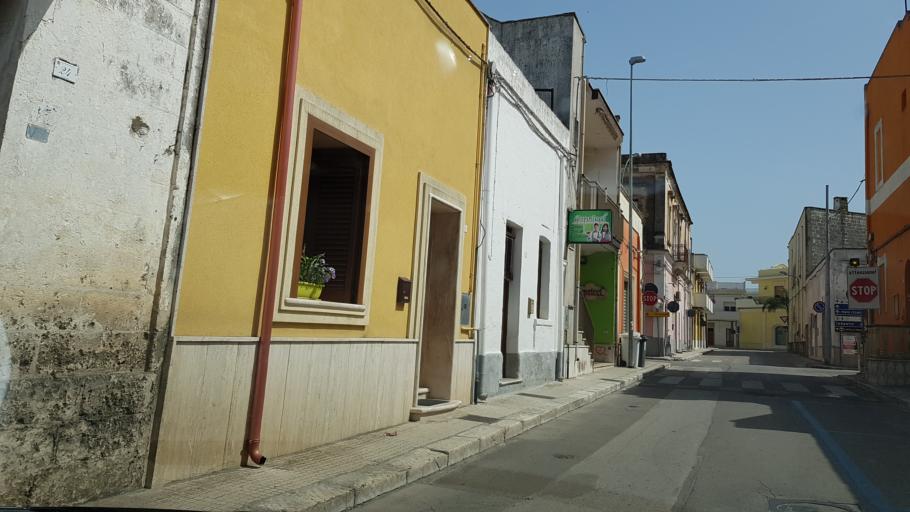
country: IT
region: Apulia
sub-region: Provincia di Brindisi
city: San Pancrazio Salentino
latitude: 40.4188
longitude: 17.8406
